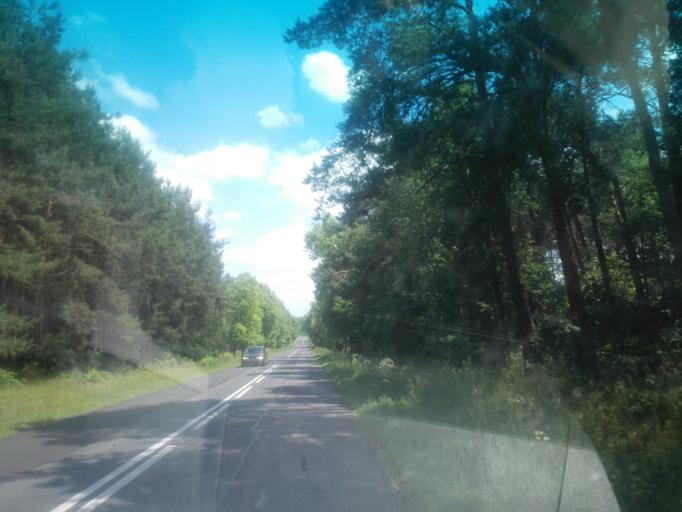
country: PL
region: Silesian Voivodeship
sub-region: Powiat czestochowski
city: Potok Zloty
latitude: 50.7383
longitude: 19.3624
